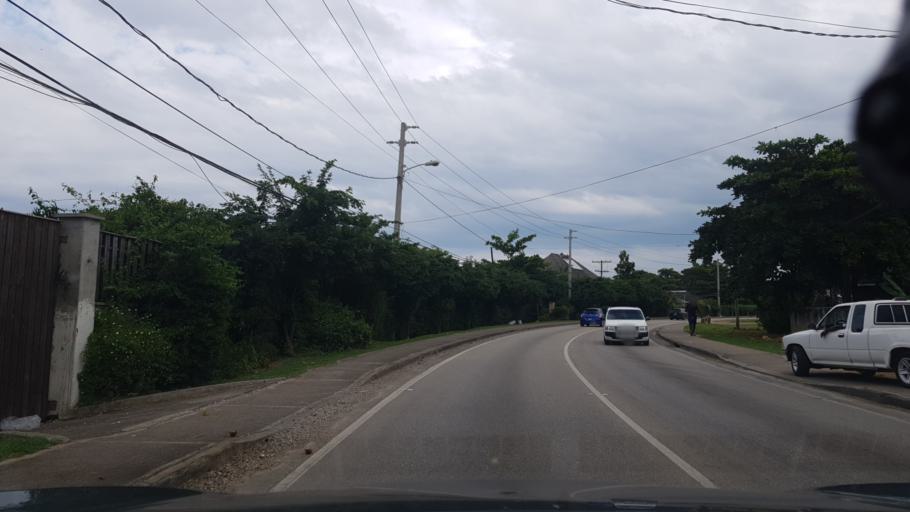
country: JM
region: Saint Ann
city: Runaway Bay
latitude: 18.4629
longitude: -77.3386
